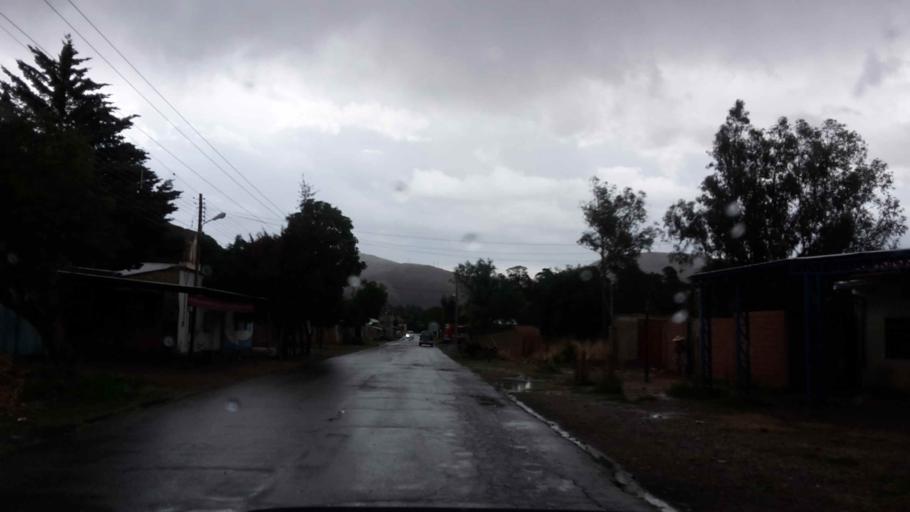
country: BO
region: Cochabamba
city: Tarata
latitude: -17.5463
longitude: -66.1018
